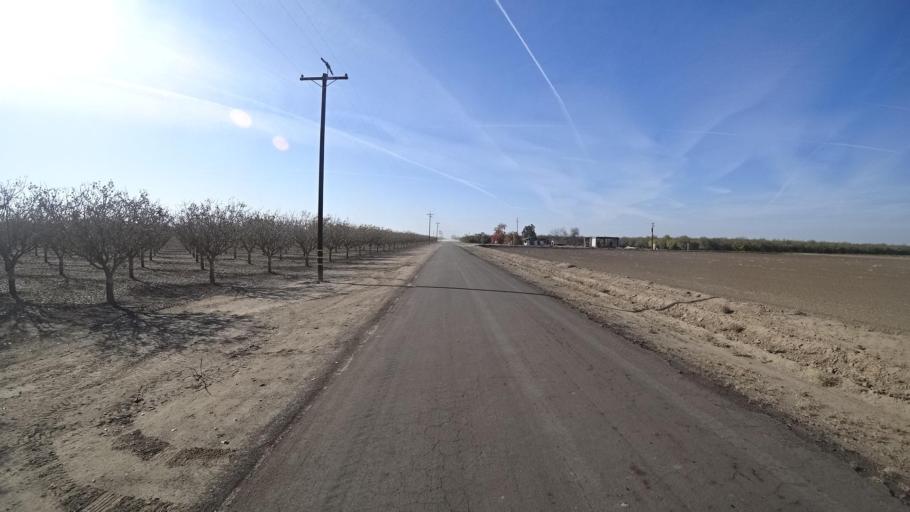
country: US
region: California
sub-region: Kern County
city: Wasco
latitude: 35.6887
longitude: -119.3960
